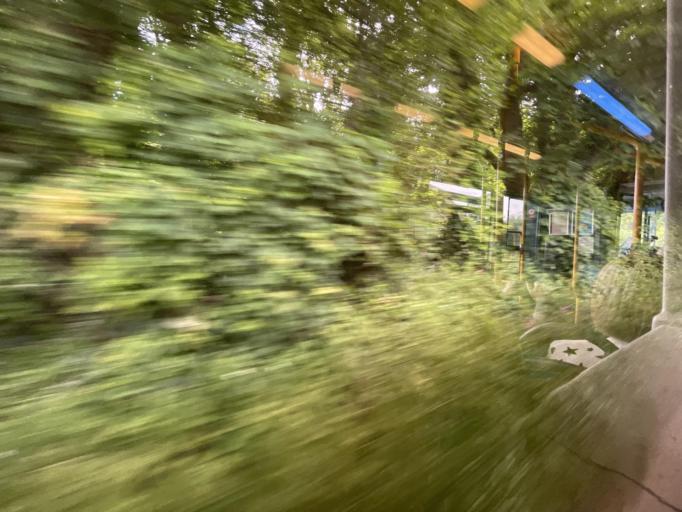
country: GB
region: Wales
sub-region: Anglesey
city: Beaumaris
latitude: 53.2669
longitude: -4.1137
